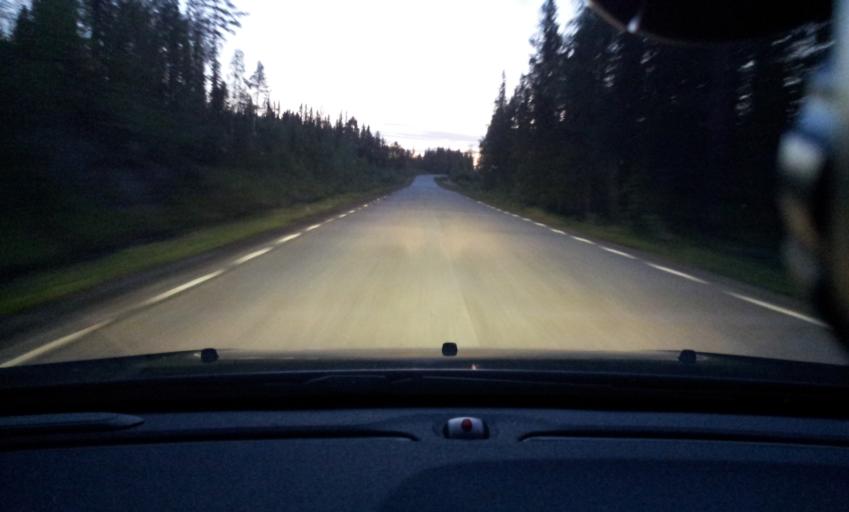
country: SE
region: Jaemtland
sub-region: Bergs Kommun
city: Hoverberg
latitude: 62.6927
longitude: 14.6308
